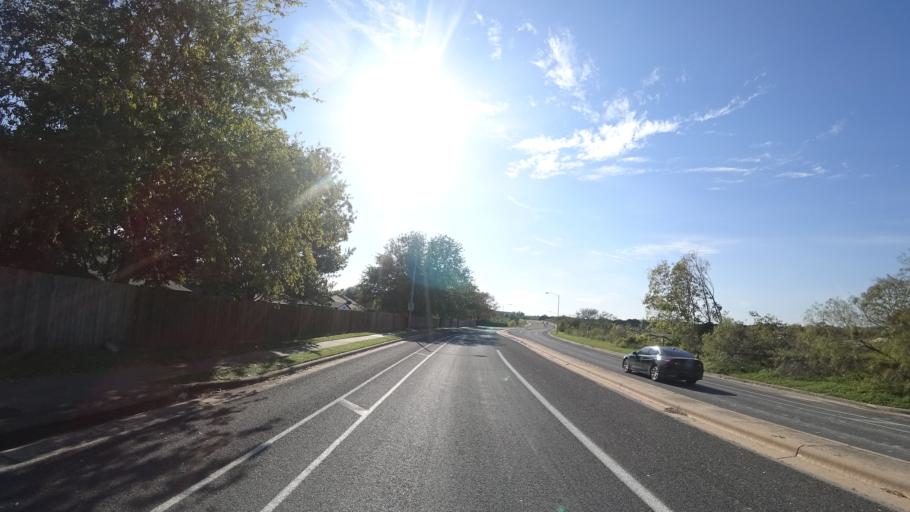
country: US
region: Texas
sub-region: Travis County
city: Pflugerville
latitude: 30.4056
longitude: -97.6516
